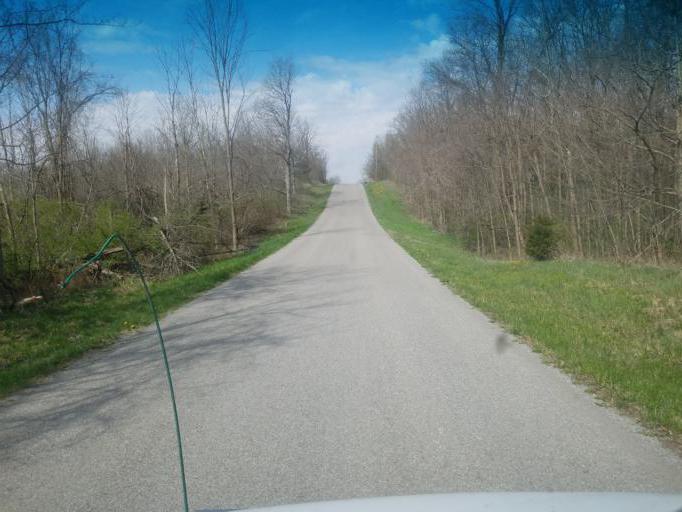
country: US
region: Ohio
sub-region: Logan County
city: Northwood
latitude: 40.4964
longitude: -83.6781
